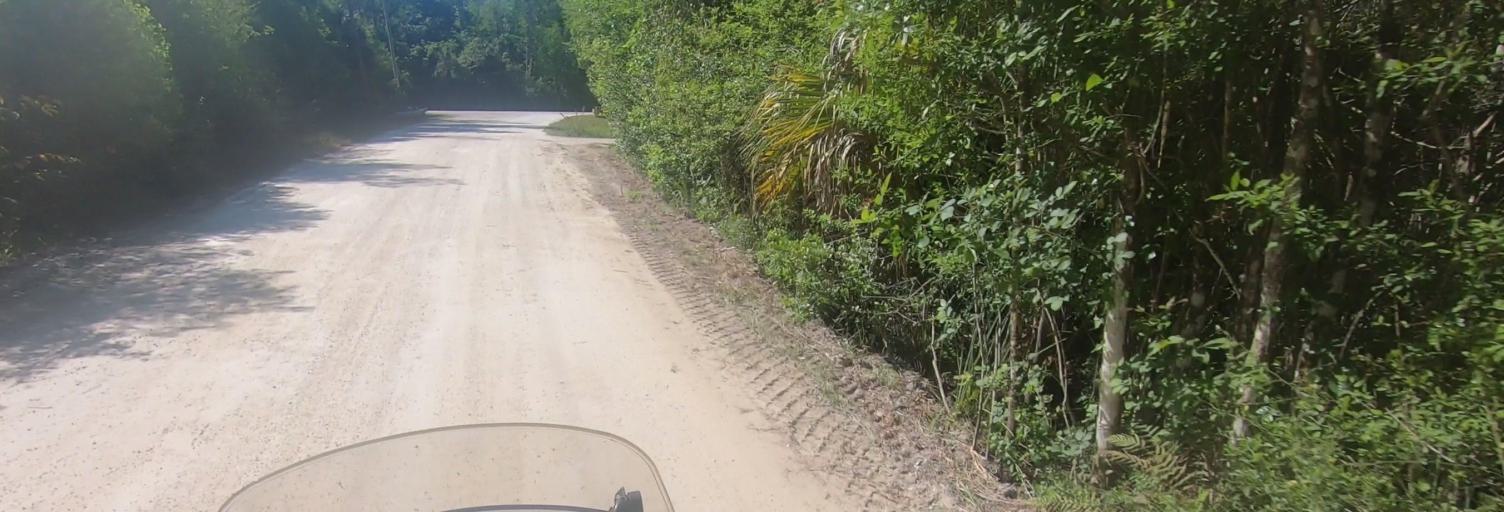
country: US
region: Florida
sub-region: Collier County
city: Marco
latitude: 25.8777
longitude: -81.2300
